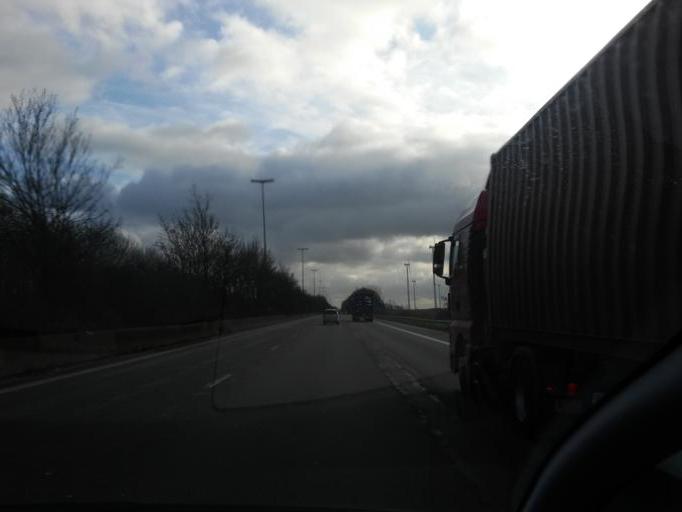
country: BE
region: Wallonia
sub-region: Province du Brabant Wallon
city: Perwez
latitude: 50.6134
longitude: 4.7736
